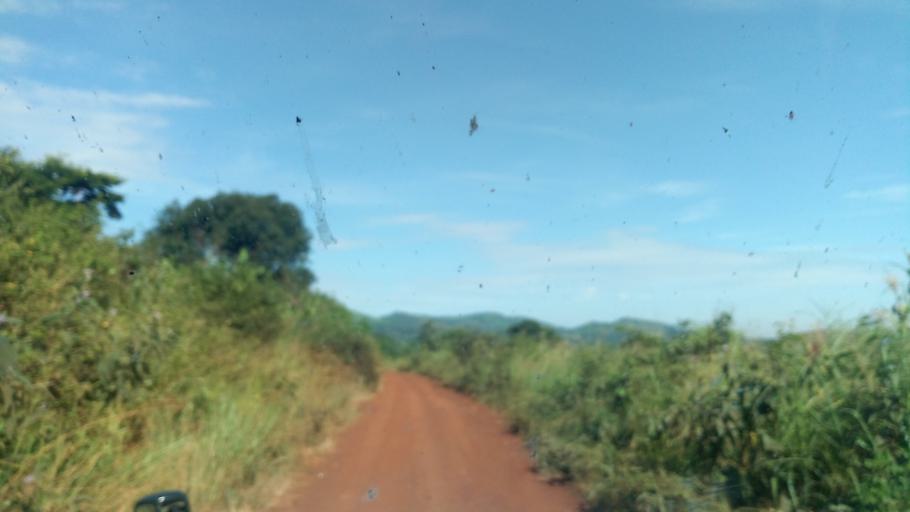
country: UG
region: Western Region
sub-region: Masindi District
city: Masindi
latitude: 1.6432
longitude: 31.7657
